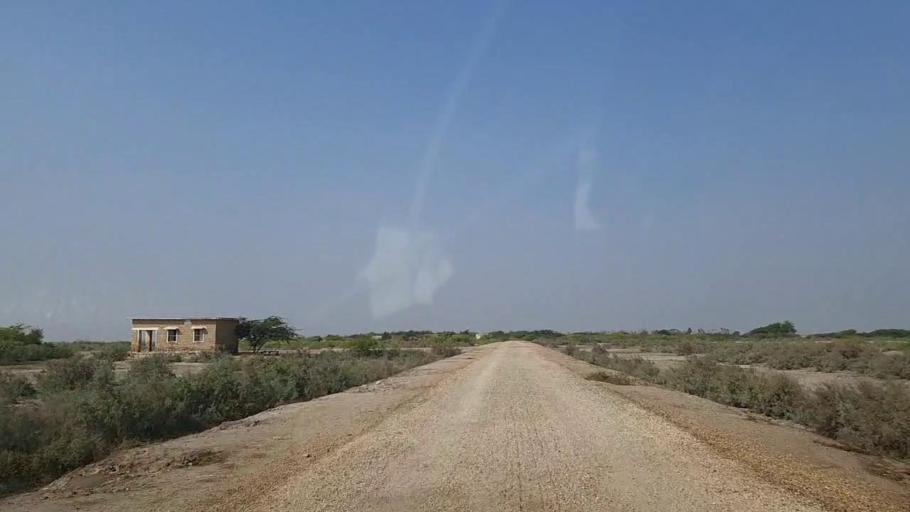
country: PK
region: Sindh
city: Mirpur Sakro
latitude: 24.6590
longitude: 67.7266
